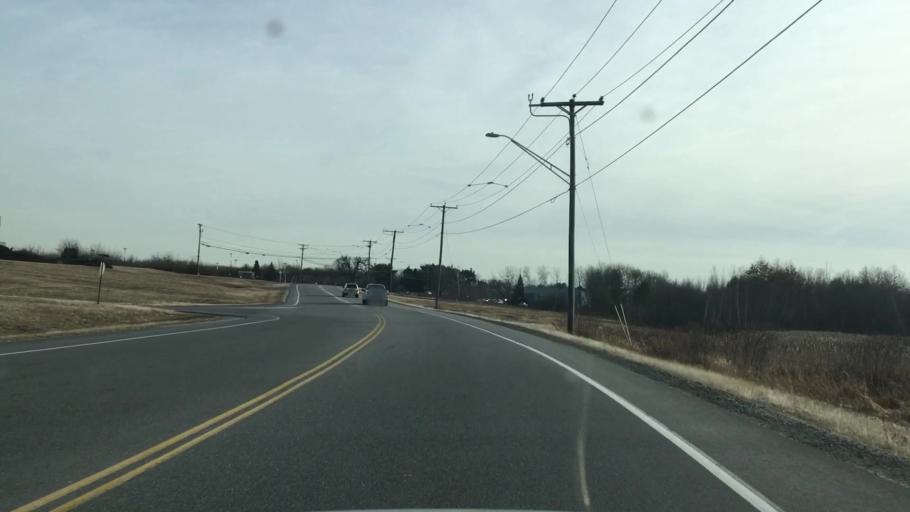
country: US
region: New Hampshire
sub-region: Rockingham County
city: Londonderry
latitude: 42.9137
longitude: -71.4239
